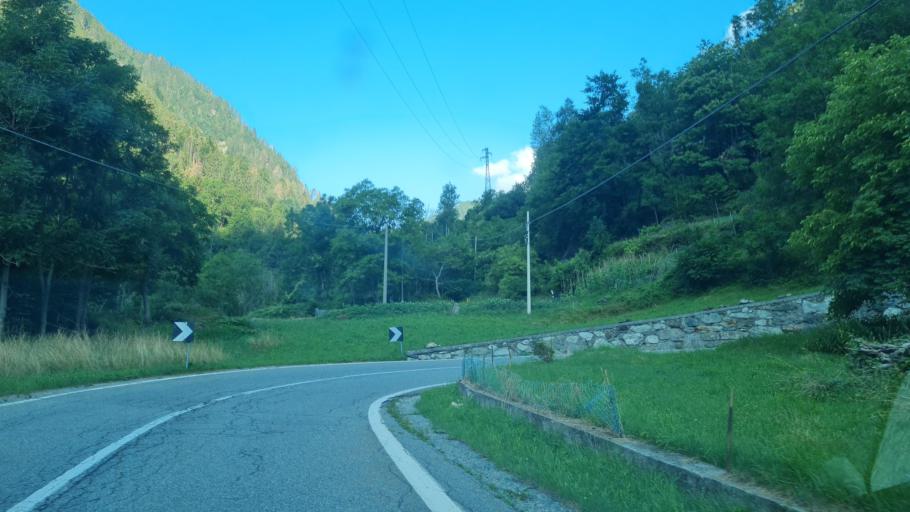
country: IT
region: Aosta Valley
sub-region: Valle d'Aosta
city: Pont-Bozet
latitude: 45.6169
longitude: 7.6735
